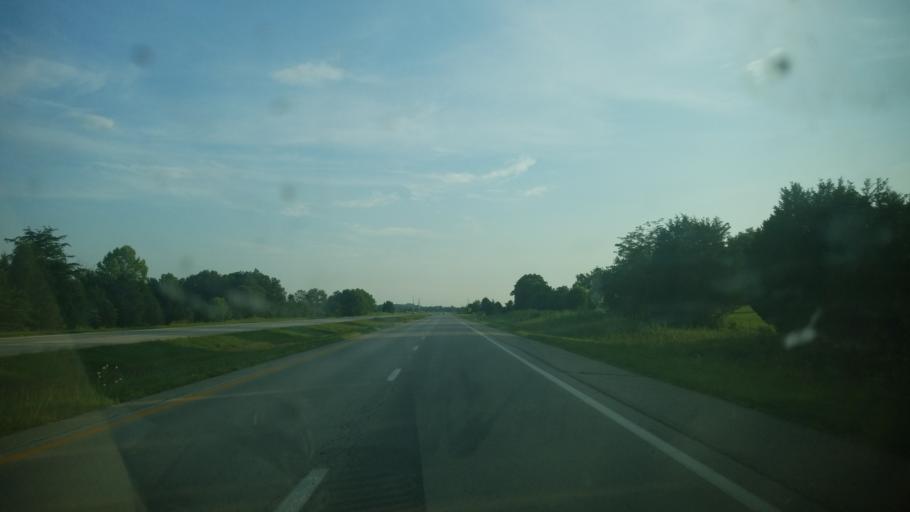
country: US
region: Ohio
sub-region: Adams County
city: Peebles
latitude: 38.9636
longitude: -83.3544
